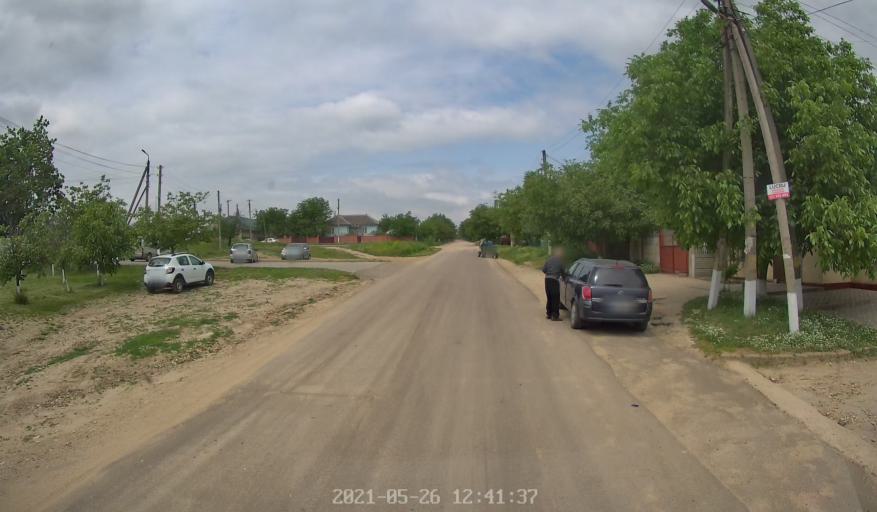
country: MD
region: Hincesti
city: Dancu
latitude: 46.7680
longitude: 28.3371
